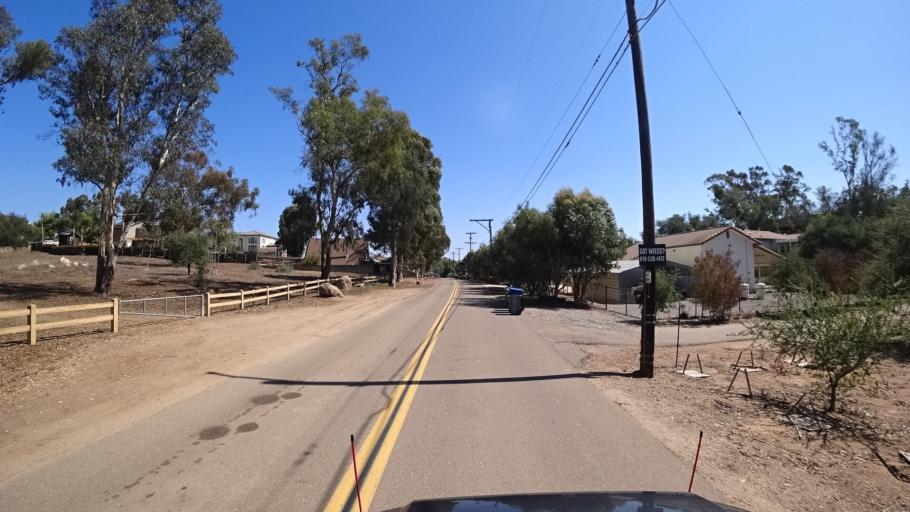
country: US
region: California
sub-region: San Diego County
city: Crest
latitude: 32.8008
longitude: -116.8664
